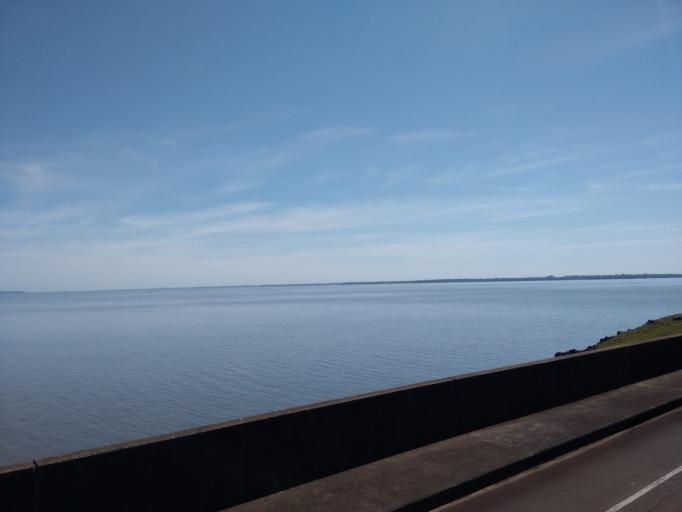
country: PY
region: Alto Parana
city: Ciudad del Este
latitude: -25.4095
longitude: -54.5785
